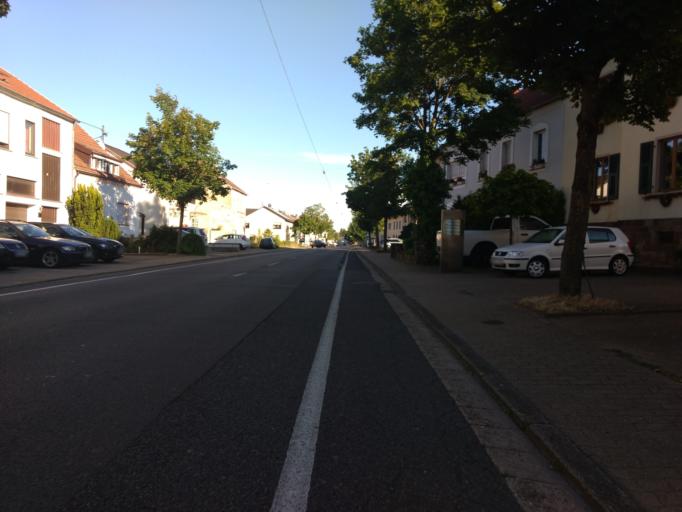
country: DE
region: Saarland
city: Rehlingen-Siersburg
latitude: 49.3770
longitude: 6.6793
